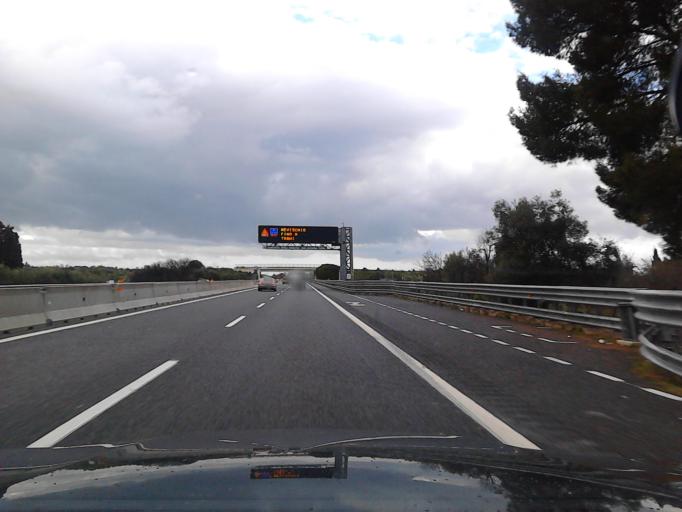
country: IT
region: Apulia
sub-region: Provincia di Bari
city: Molfetta
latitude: 41.1725
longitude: 16.5929
